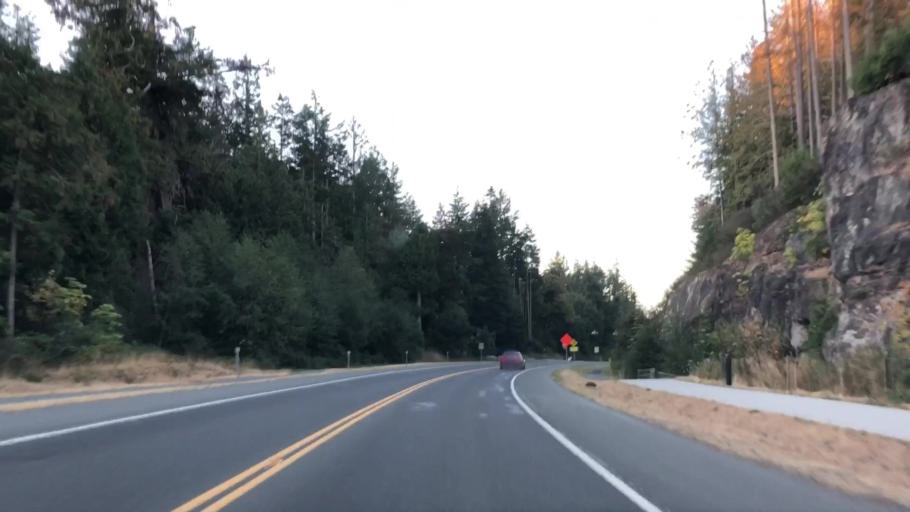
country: CA
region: British Columbia
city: Colwood
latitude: 48.4155
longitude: -123.5047
